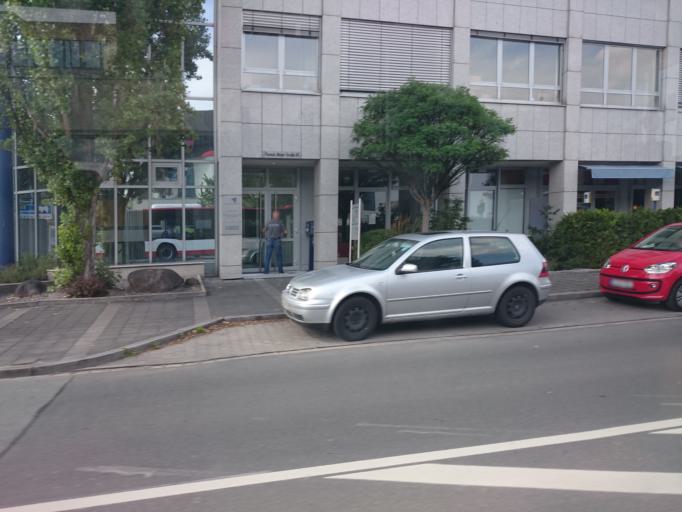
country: DE
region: Bavaria
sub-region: Regierungsbezirk Mittelfranken
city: Wendelstein
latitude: 49.4135
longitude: 11.1360
